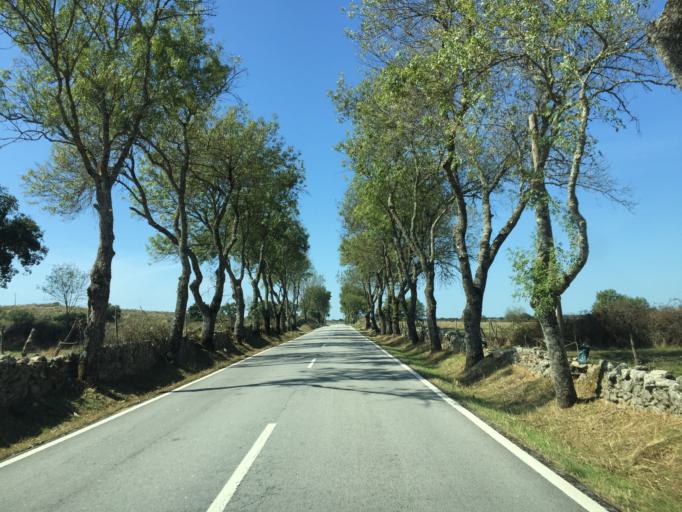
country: PT
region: Portalegre
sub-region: Portalegre
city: Alagoa
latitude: 39.4379
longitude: -7.5685
